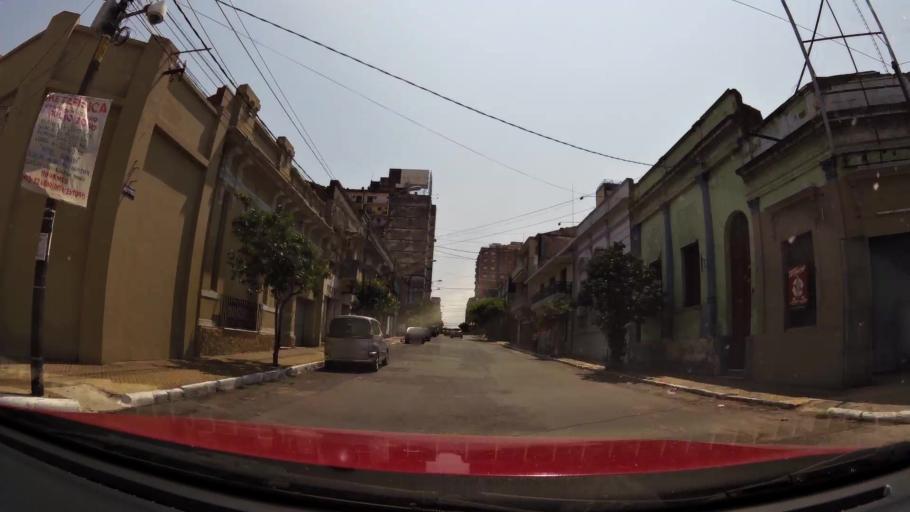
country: PY
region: Asuncion
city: Asuncion
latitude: -25.2818
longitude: -57.6418
